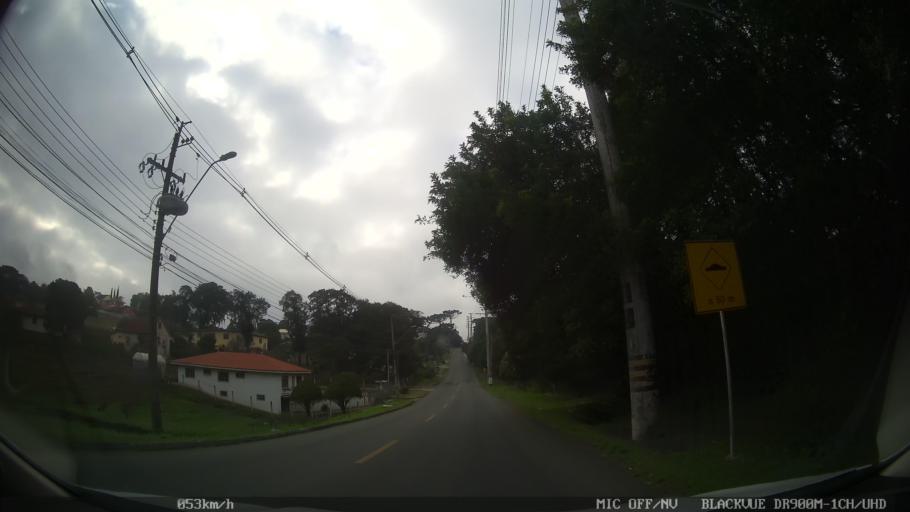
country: BR
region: Parana
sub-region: Curitiba
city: Curitiba
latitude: -25.3935
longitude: -49.3242
